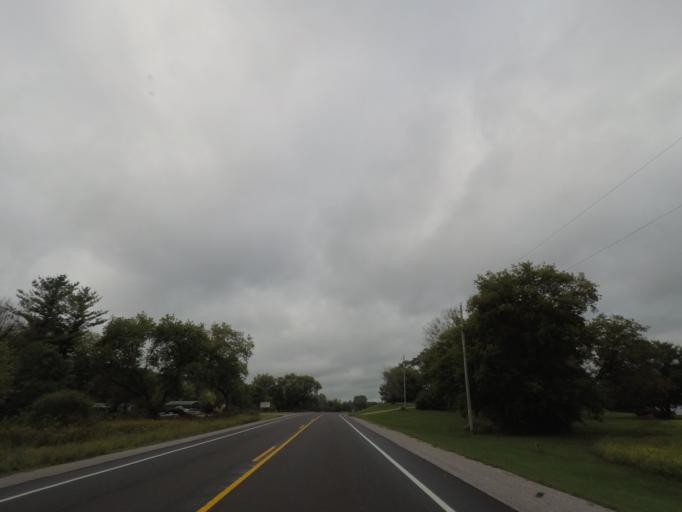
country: US
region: Wisconsin
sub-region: Jefferson County
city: Ixonia
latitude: 43.0124
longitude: -88.6045
